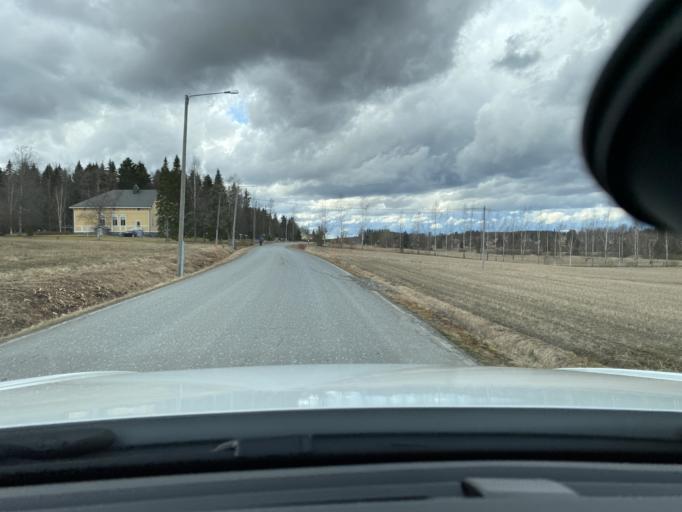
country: FI
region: Pirkanmaa
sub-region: Lounais-Pirkanmaa
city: Punkalaidun
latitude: 61.1112
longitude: 23.0955
